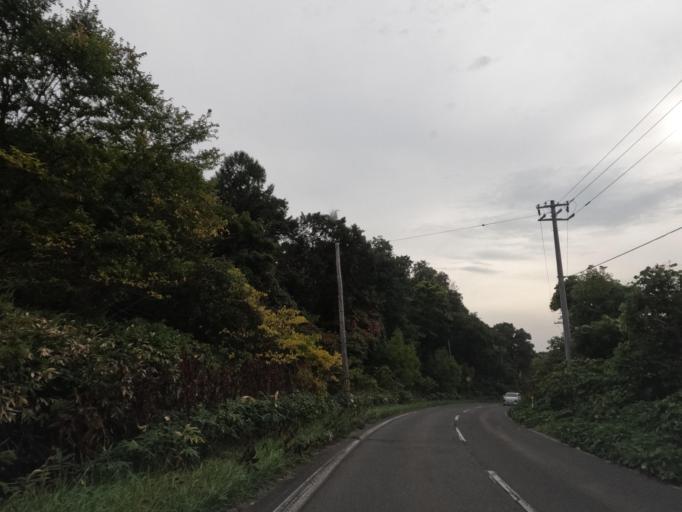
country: JP
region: Hokkaido
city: Date
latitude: 42.4636
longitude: 140.9066
